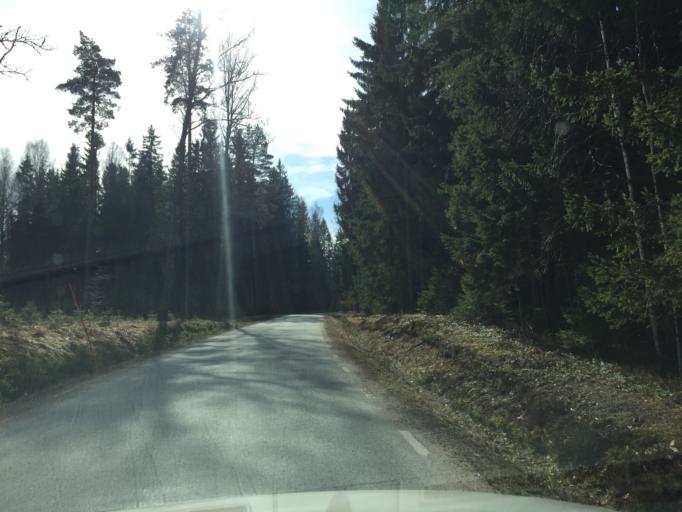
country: SE
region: OErebro
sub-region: Orebro Kommun
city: Hovsta
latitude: 59.3813
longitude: 15.1747
